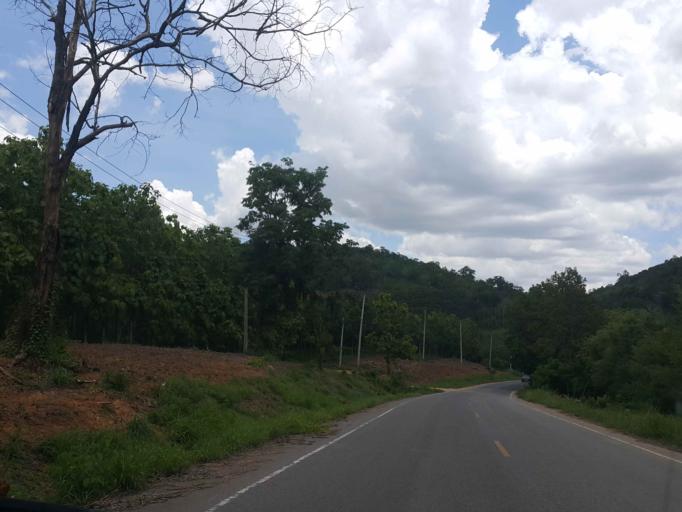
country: TH
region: Nan
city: Wiang Sa
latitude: 18.5399
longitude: 100.5473
